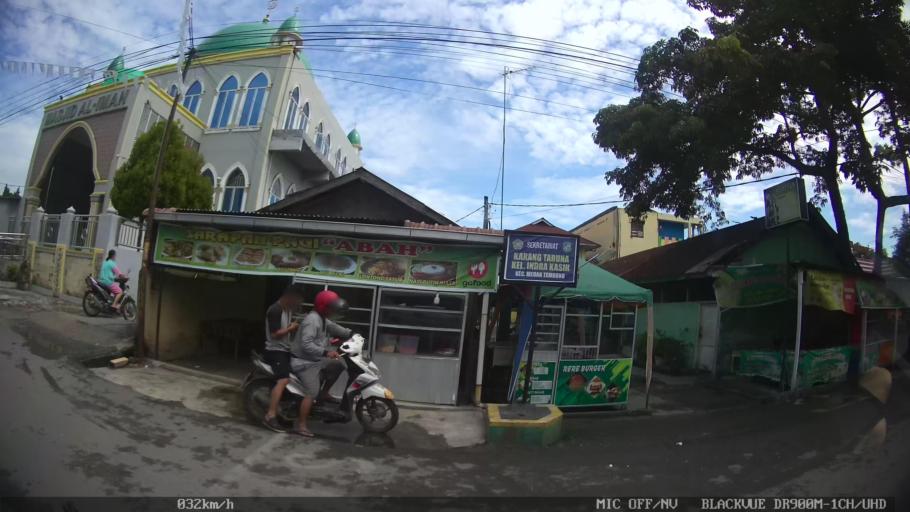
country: ID
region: North Sumatra
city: Medan
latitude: 3.6229
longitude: 98.7042
